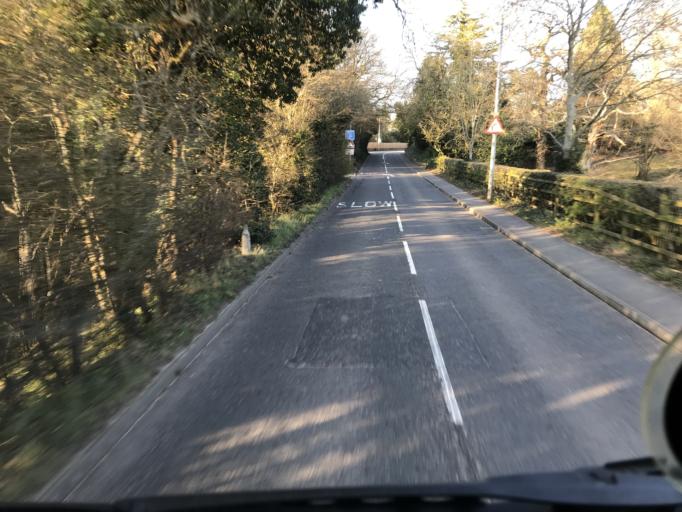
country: GB
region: England
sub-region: Cheshire East
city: Wilmslow
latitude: 53.3267
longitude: -2.2117
